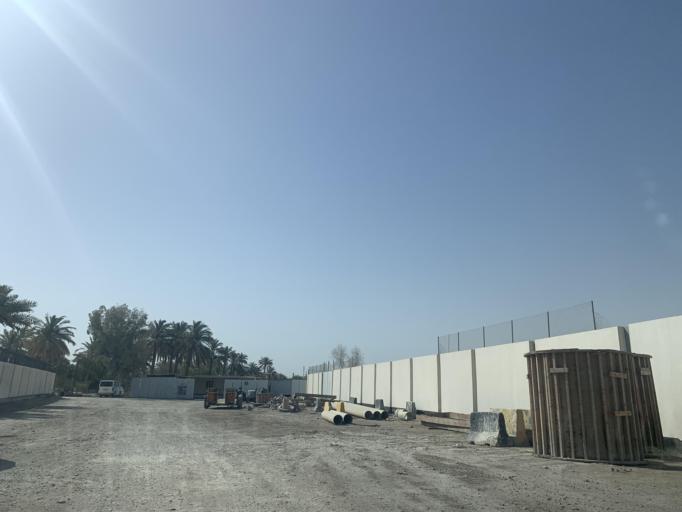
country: BH
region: Manama
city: Jidd Hafs
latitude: 26.2082
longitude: 50.5588
